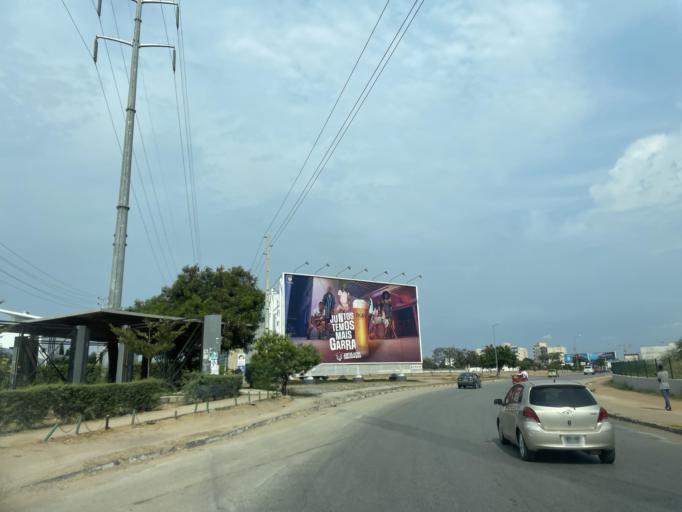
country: AO
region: Luanda
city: Luanda
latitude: -8.9208
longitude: 13.1893
